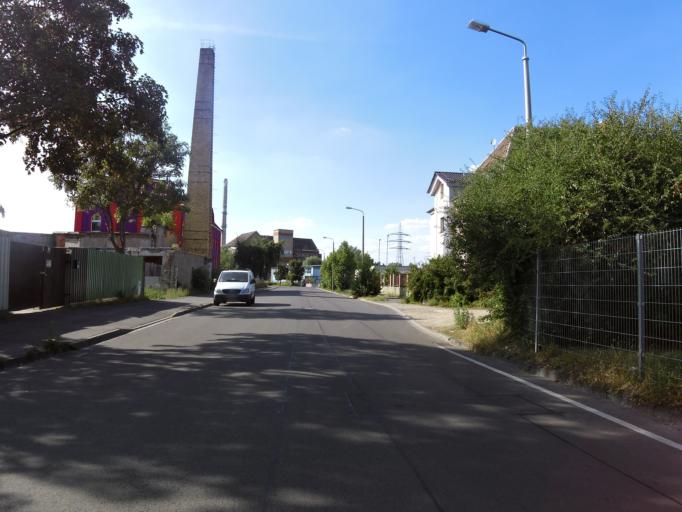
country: DE
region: Saxony
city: Leipzig
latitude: 51.3448
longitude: 12.3034
